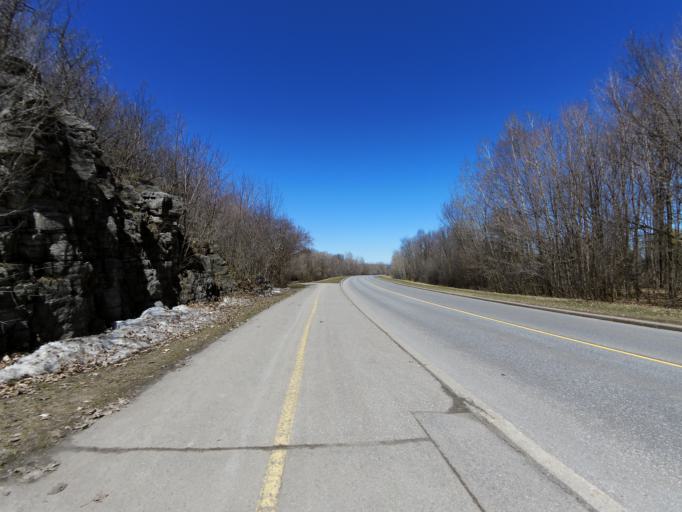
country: CA
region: Quebec
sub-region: Outaouais
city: Gatineau
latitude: 45.4481
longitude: -75.6453
